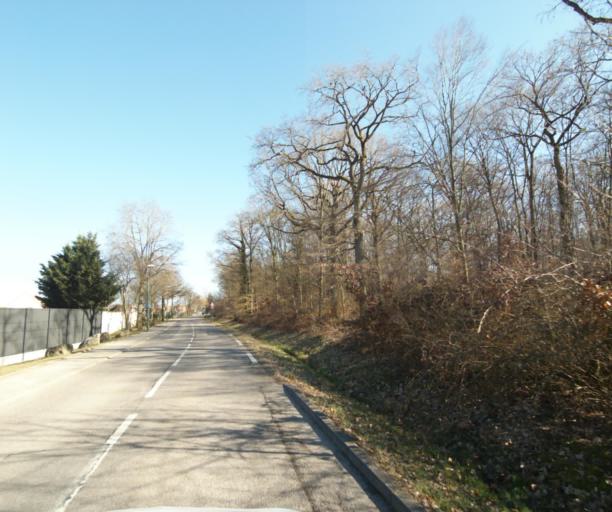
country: FR
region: Lorraine
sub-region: Departement de Meurthe-et-Moselle
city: Saulxures-les-Nancy
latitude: 48.6760
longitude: 6.2358
